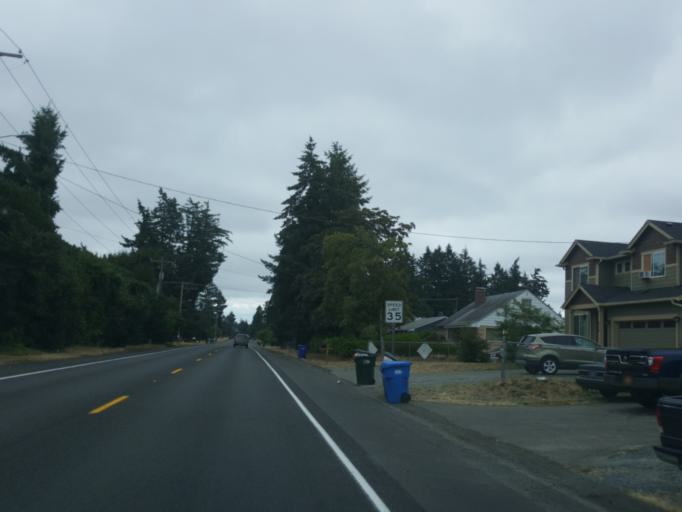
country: US
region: Washington
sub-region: Pierce County
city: Parkland
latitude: 47.1314
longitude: -122.4474
